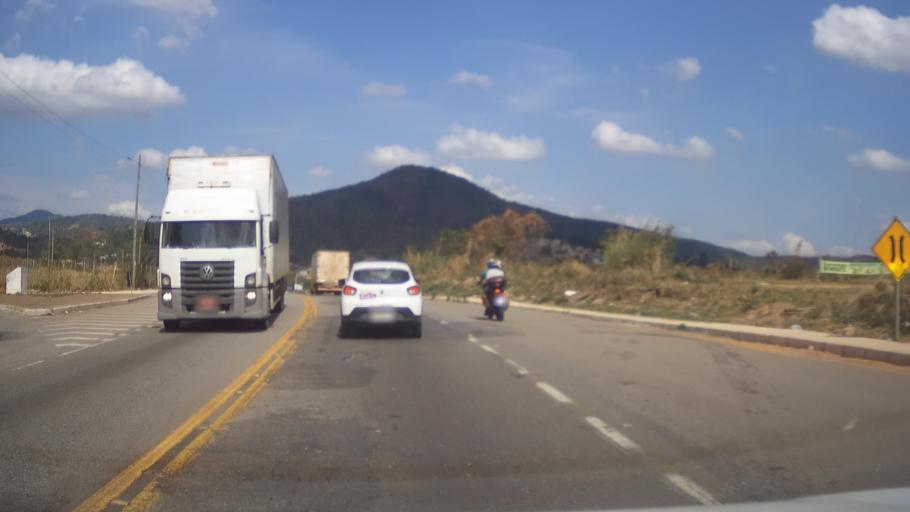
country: BR
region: Minas Gerais
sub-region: Santa Luzia
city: Santa Luzia
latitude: -19.8405
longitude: -43.8739
